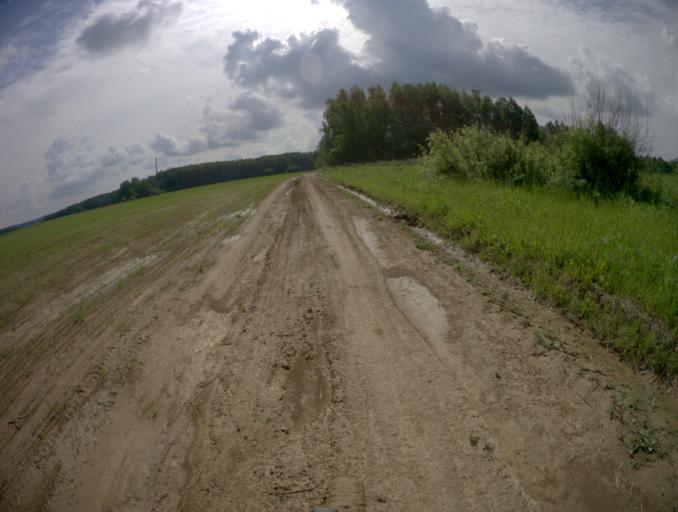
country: RU
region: Vladimir
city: Lakinsk
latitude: 56.0962
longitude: 39.9148
